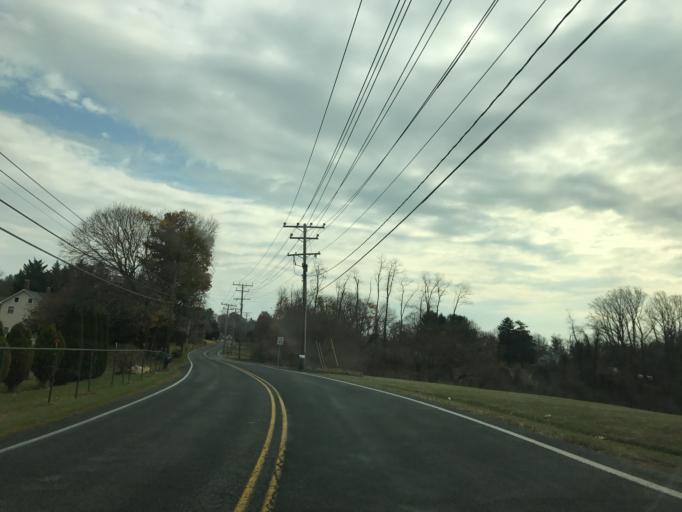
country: US
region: Maryland
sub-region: Harford County
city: Jarrettsville
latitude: 39.5941
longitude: -76.4388
